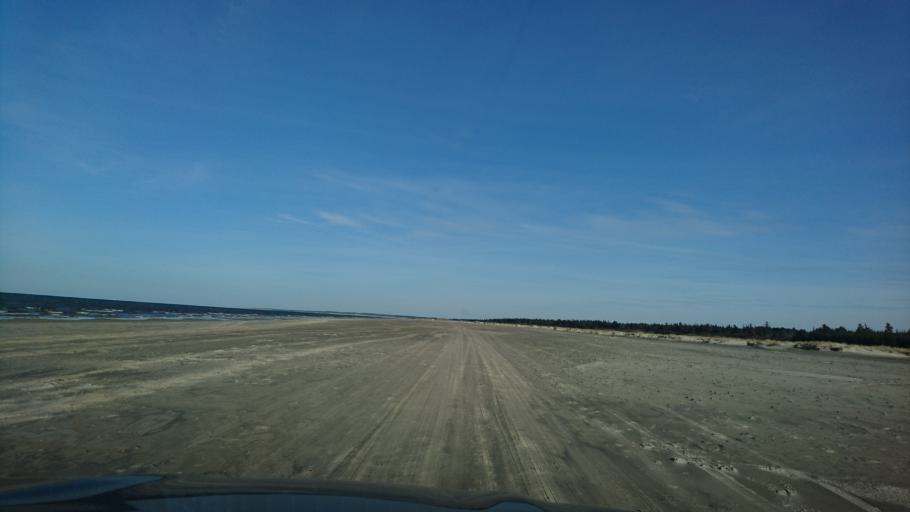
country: DK
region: North Denmark
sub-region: Hjorring Kommune
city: Hirtshals
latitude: 57.5897
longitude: 10.0817
